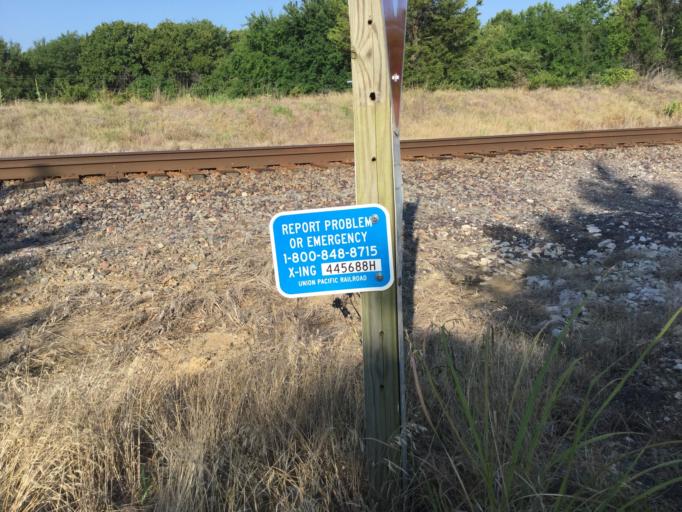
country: US
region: Kansas
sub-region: Montgomery County
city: Coffeyville
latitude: 37.0852
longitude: -95.7469
